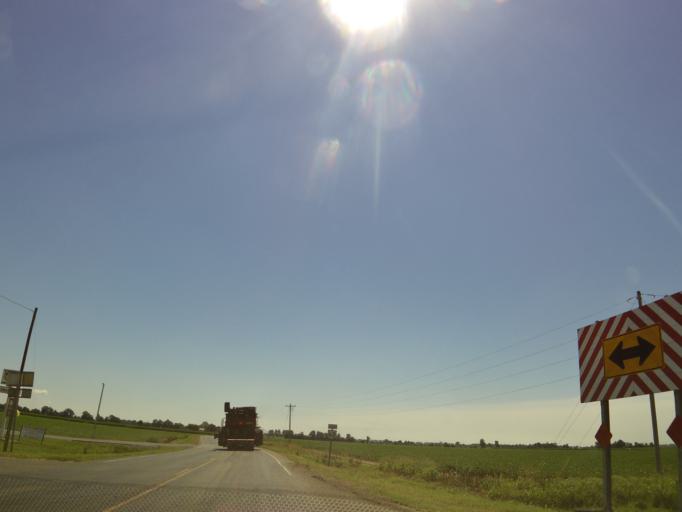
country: US
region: Missouri
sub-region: New Madrid County
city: Gideon
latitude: 36.5535
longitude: -89.8095
